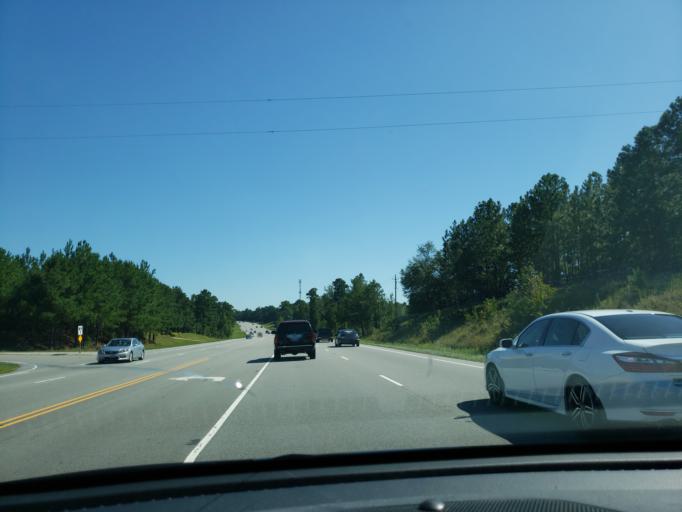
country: US
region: North Carolina
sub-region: Lee County
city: Broadway
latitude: 35.3520
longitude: -79.1089
